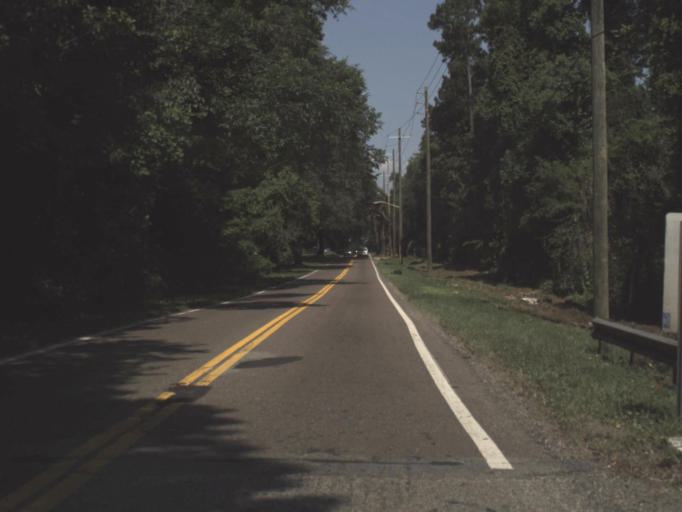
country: US
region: Florida
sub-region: Duval County
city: Jacksonville
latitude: 30.3645
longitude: -81.7381
